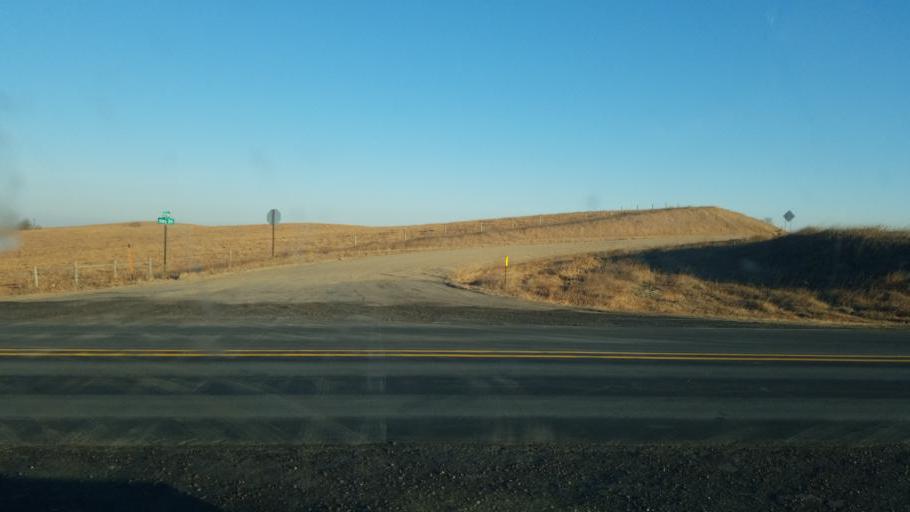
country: US
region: Nebraska
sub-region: Knox County
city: Center
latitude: 42.5970
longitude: -97.7802
